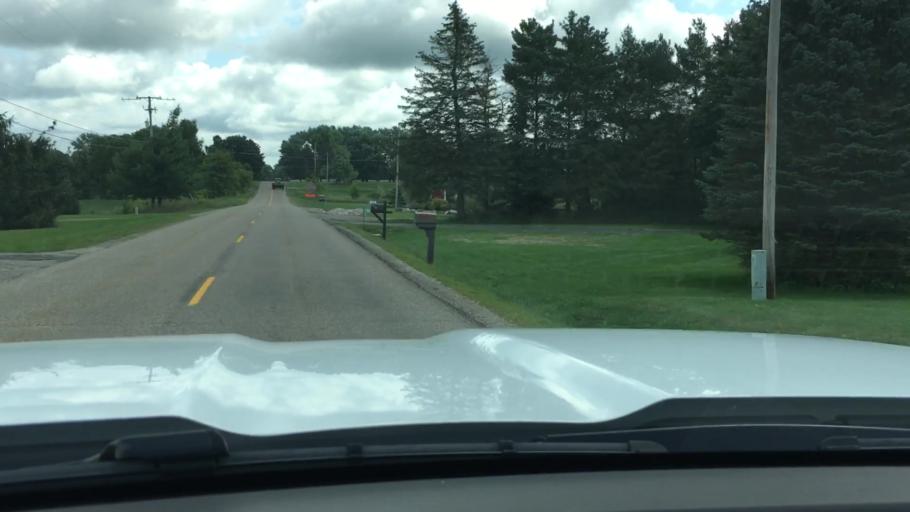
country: US
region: Michigan
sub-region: Eaton County
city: Dimondale
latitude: 42.5820
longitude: -84.6194
